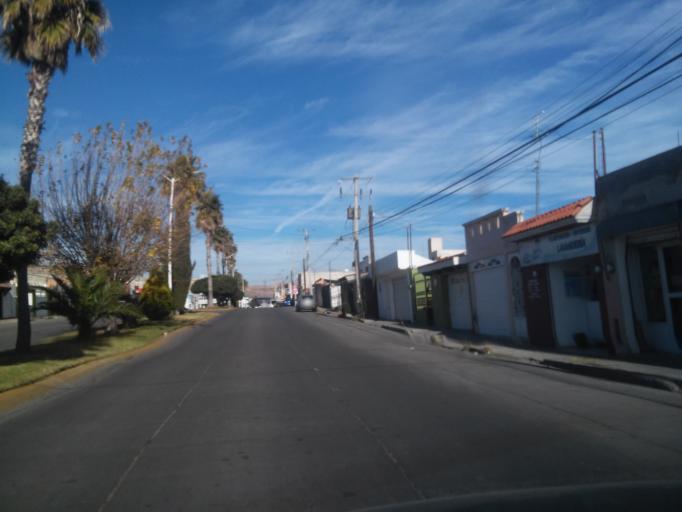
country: MX
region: Durango
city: Victoria de Durango
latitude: 24.0388
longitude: -104.6555
